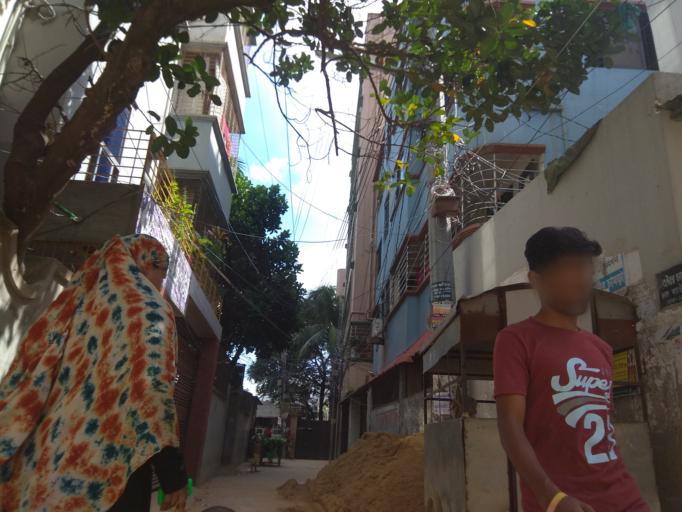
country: BD
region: Dhaka
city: Tungi
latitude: 23.8147
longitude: 90.3923
